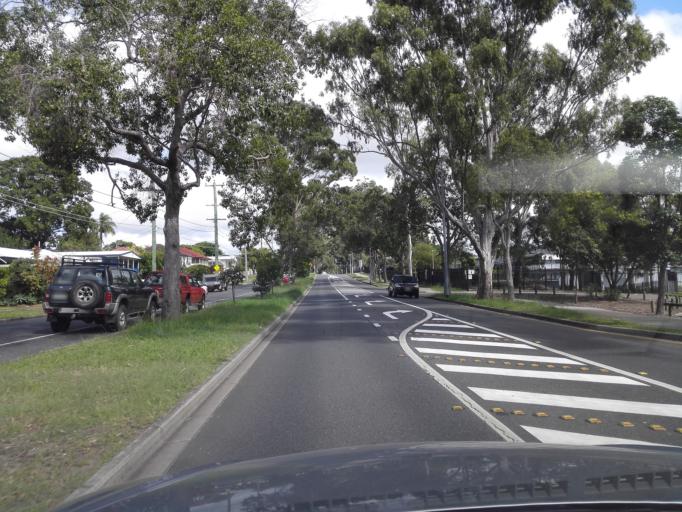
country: AU
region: Queensland
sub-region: Brisbane
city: Zillmere
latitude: -27.3575
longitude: 153.0256
